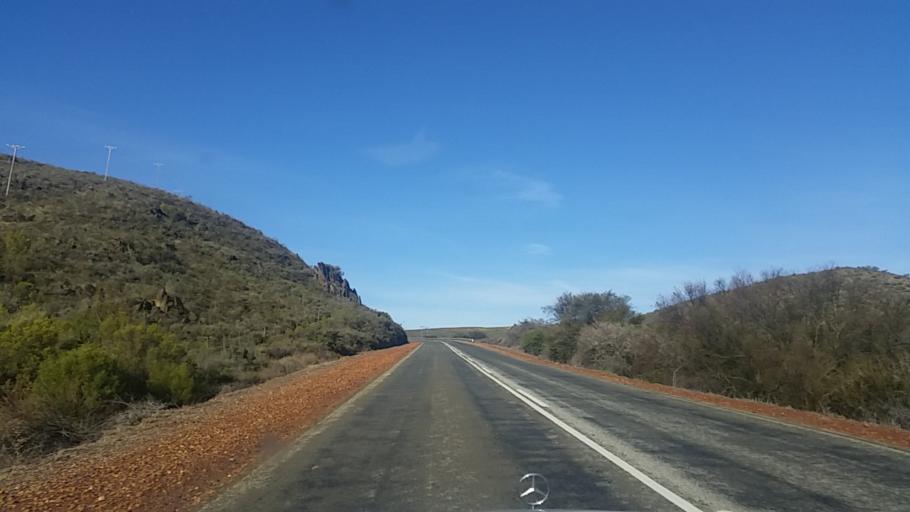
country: ZA
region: Western Cape
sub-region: Eden District Municipality
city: Knysna
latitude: -33.6909
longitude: 23.0548
